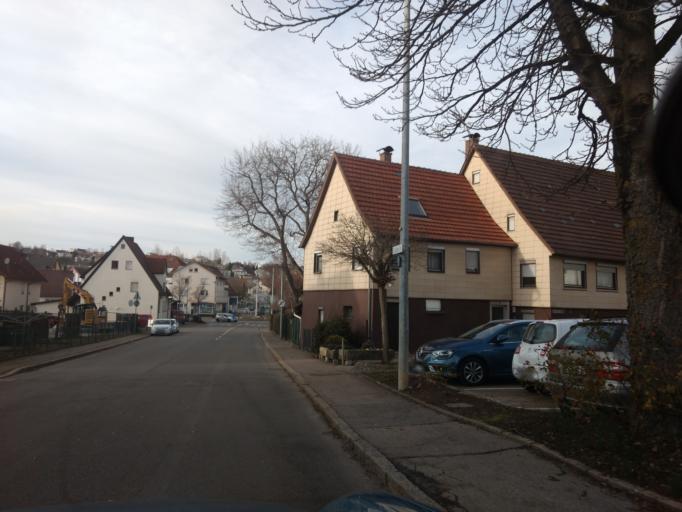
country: DE
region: Baden-Wuerttemberg
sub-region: Regierungsbezirk Stuttgart
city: Wangen
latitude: 48.7073
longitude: 9.6182
